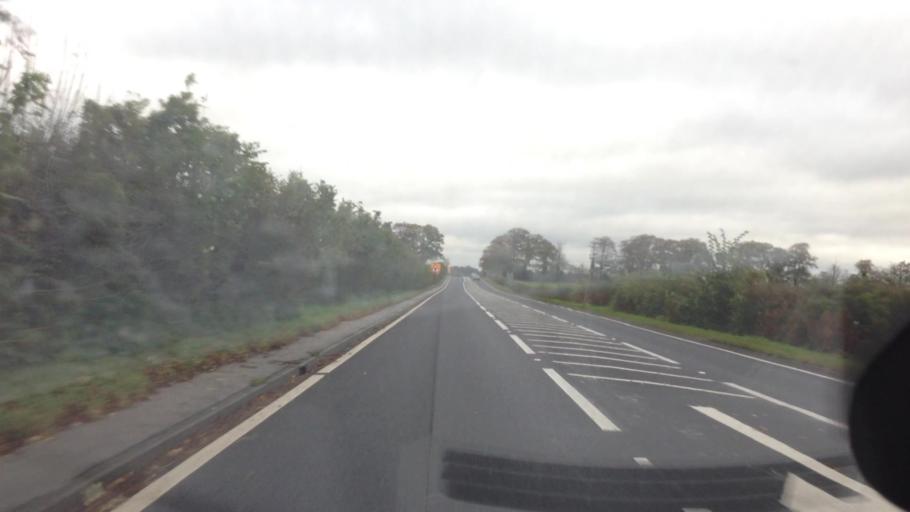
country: GB
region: England
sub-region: City and Borough of Leeds
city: Shadwell
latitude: 53.8502
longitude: -1.4643
